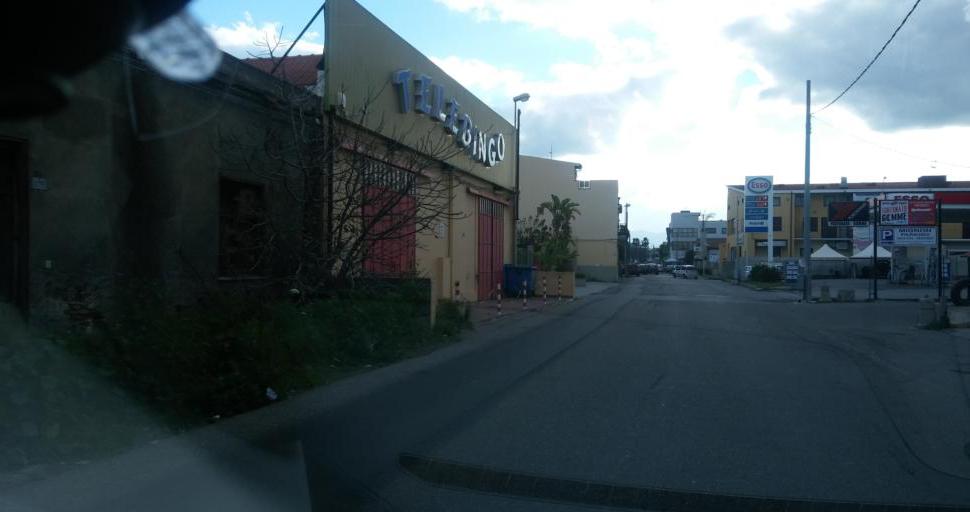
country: IT
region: Sicily
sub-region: Messina
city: Milazzo
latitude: 38.2095
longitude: 15.2513
